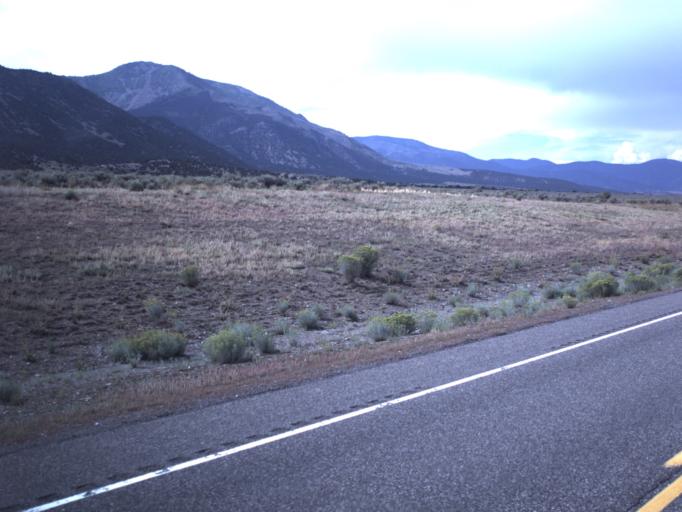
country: US
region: Utah
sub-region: Piute County
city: Junction
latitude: 38.3467
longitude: -112.2190
